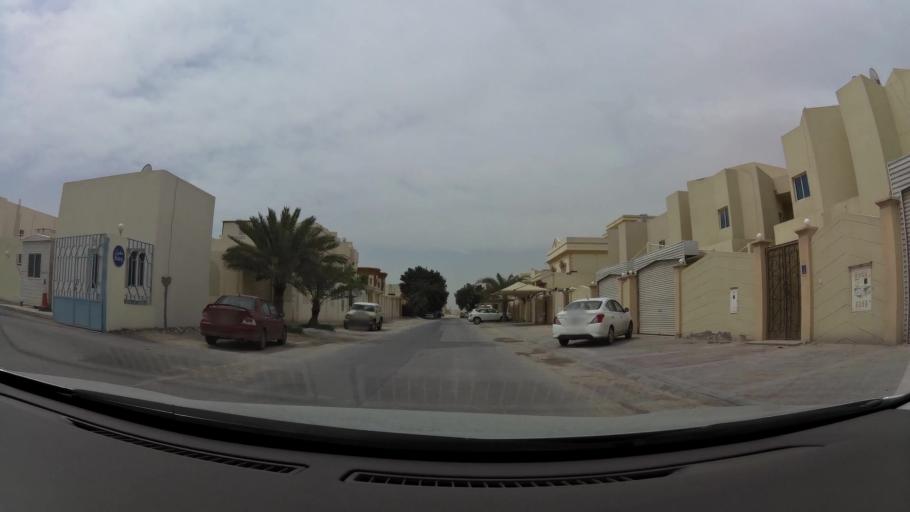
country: QA
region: Baladiyat ar Rayyan
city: Ar Rayyan
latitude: 25.2320
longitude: 51.4550
